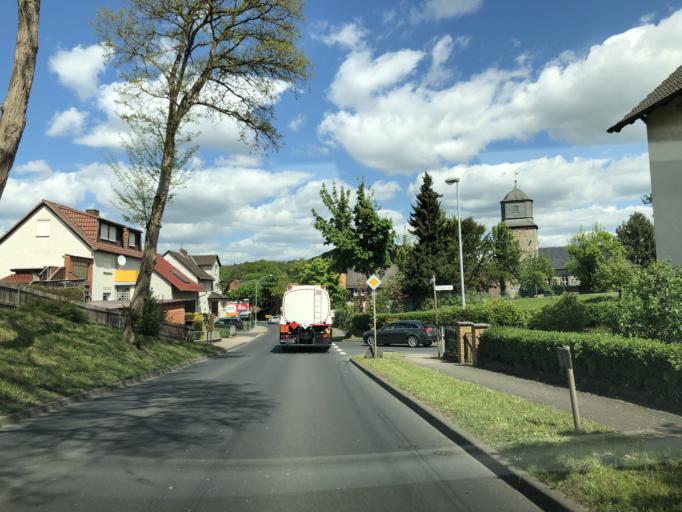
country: DE
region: Hesse
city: Felsberg
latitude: 51.1776
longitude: 9.4103
